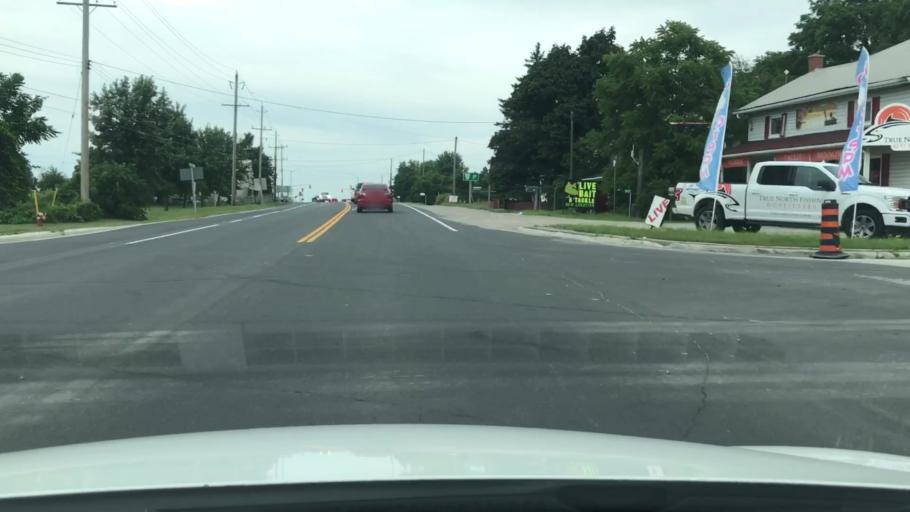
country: CA
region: Ontario
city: Bradford West Gwillimbury
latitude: 44.2126
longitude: -79.5888
